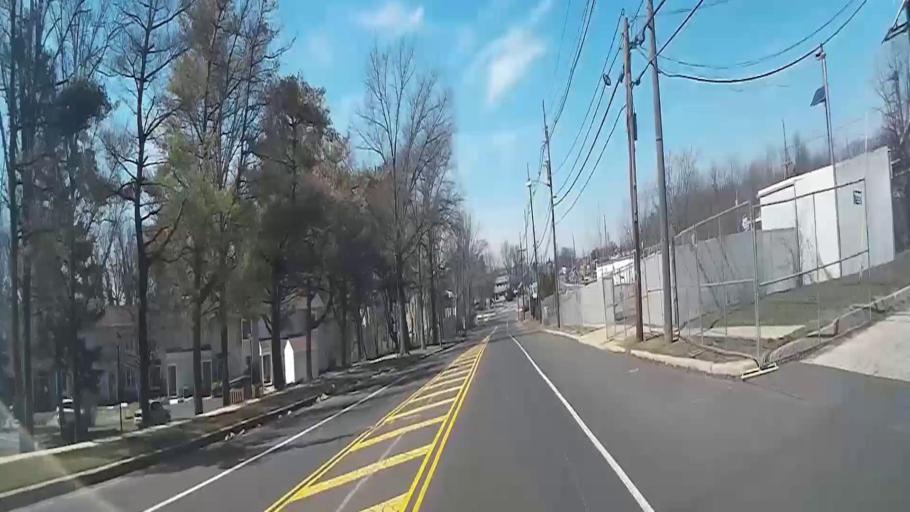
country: US
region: New Jersey
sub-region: Camden County
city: Greentree
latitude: 39.8950
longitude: -74.9436
